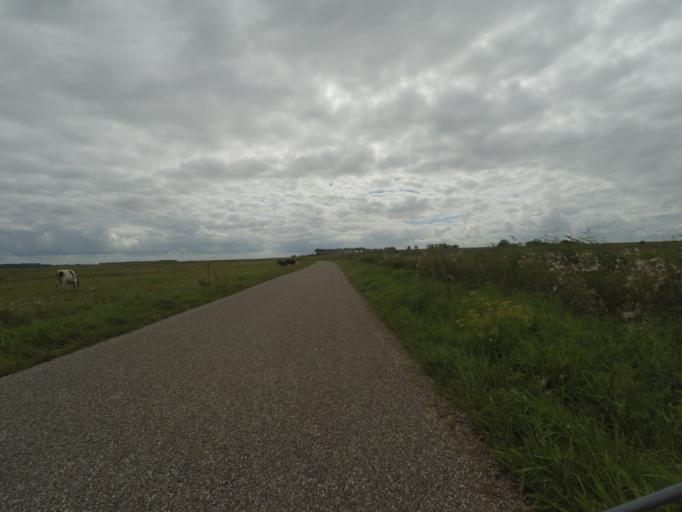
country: NL
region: Friesland
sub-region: Gemeente Dongeradeel
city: Anjum
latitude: 53.3422
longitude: 6.1529
